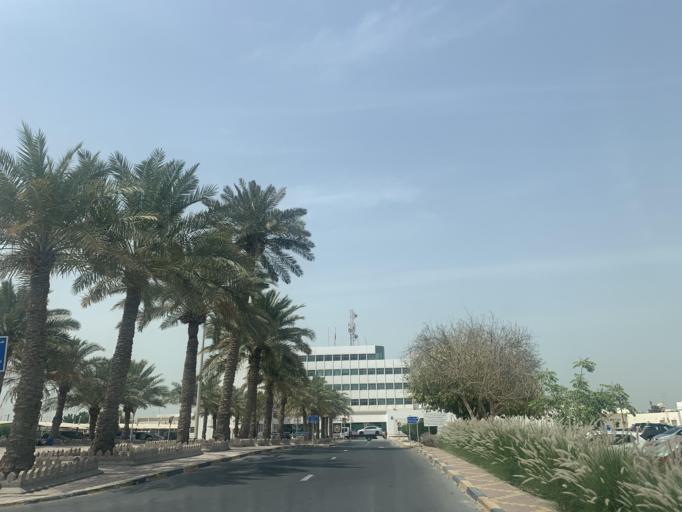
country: BH
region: Northern
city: Madinat `Isa
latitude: 26.1551
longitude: 50.5387
